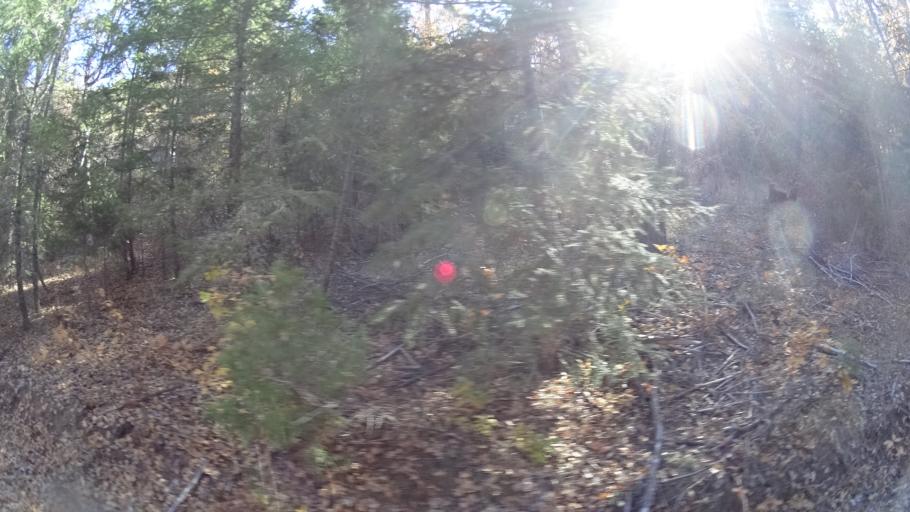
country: US
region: California
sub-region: Siskiyou County
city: Yreka
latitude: 41.8582
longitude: -122.7482
